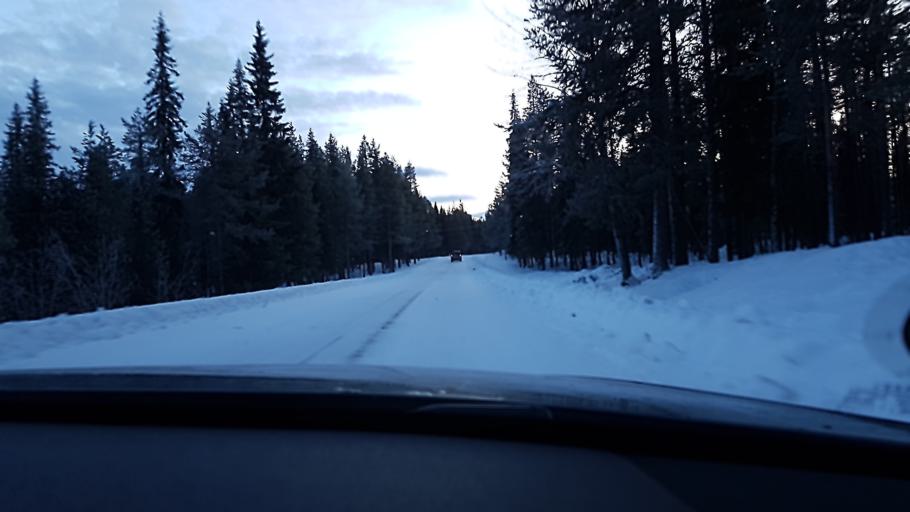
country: SE
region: Vaesterbotten
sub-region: Sorsele Kommun
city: Sorsele
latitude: 65.4994
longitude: 17.5562
